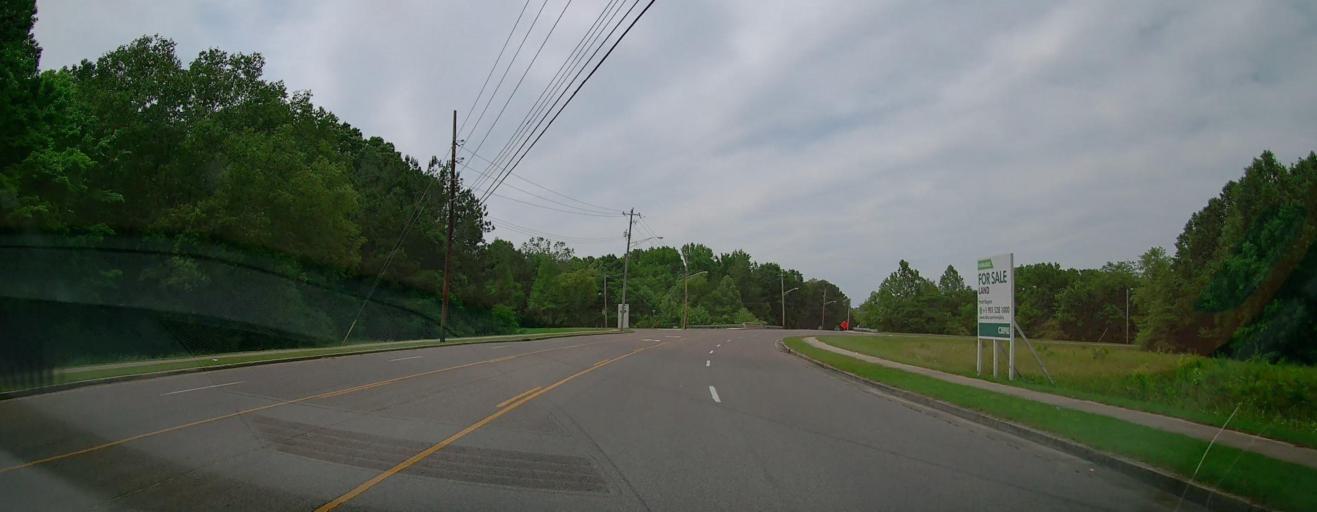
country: US
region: Tennessee
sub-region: Shelby County
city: Germantown
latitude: 35.0714
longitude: -89.8485
